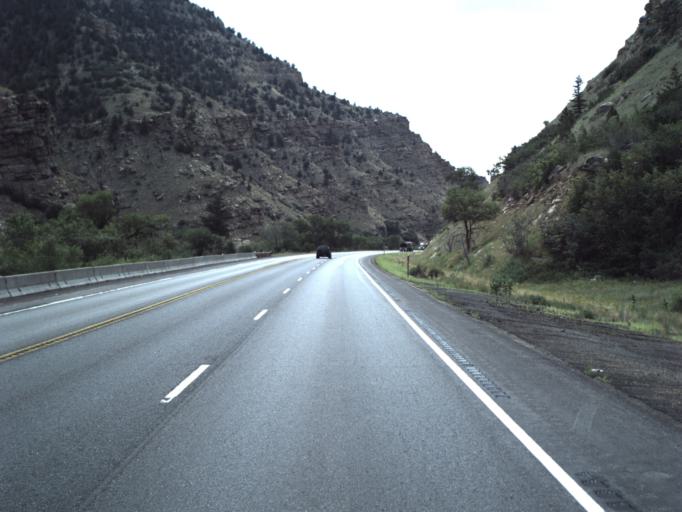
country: US
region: Utah
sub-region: Carbon County
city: Helper
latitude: 39.7606
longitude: -110.8930
